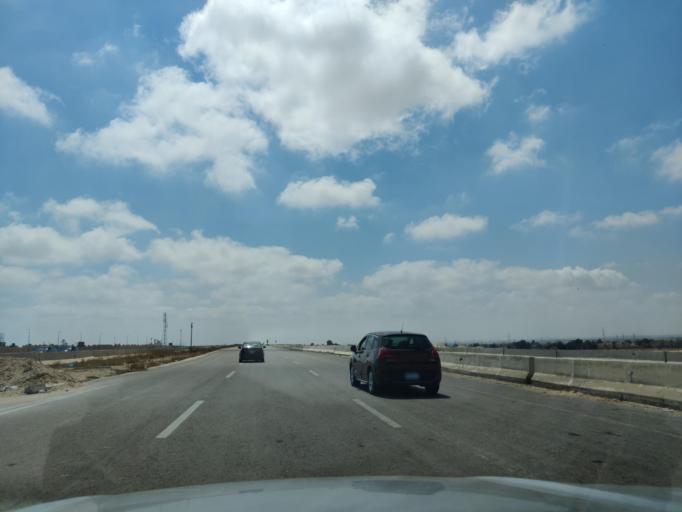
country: EG
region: Muhafazat Matruh
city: Al `Alamayn
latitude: 30.8160
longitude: 29.0350
